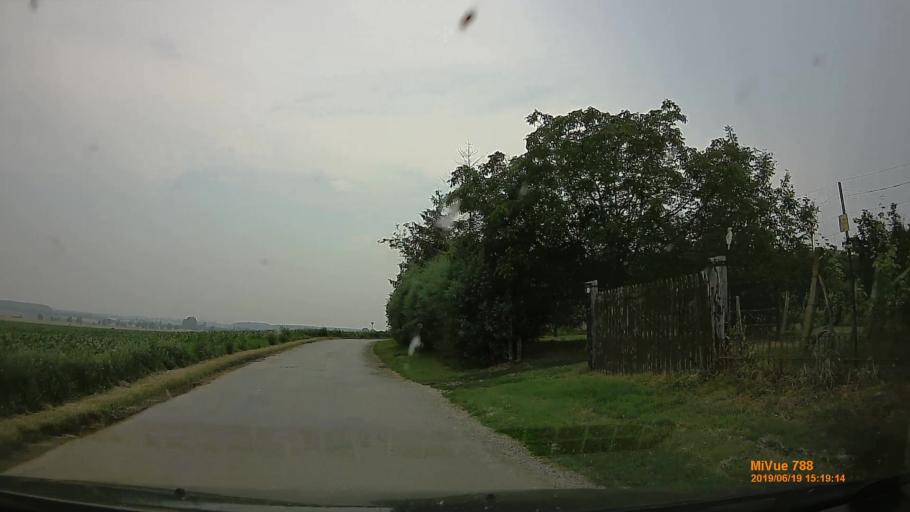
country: HU
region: Baranya
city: Szigetvar
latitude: 46.0741
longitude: 17.8552
